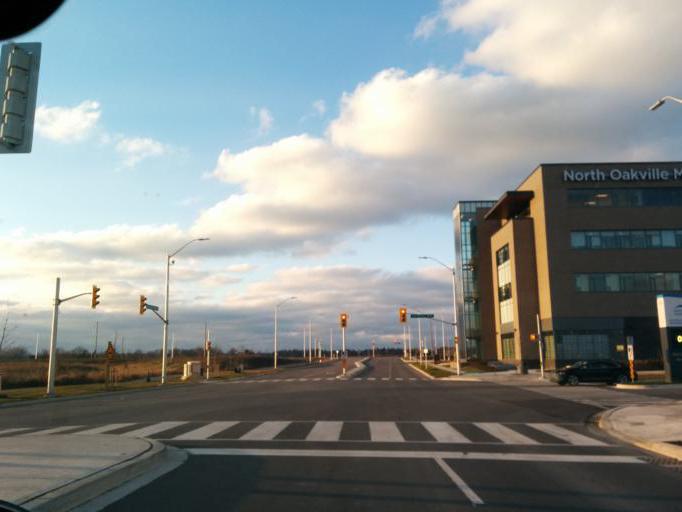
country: CA
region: Ontario
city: Oakville
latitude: 43.4487
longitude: -79.7663
